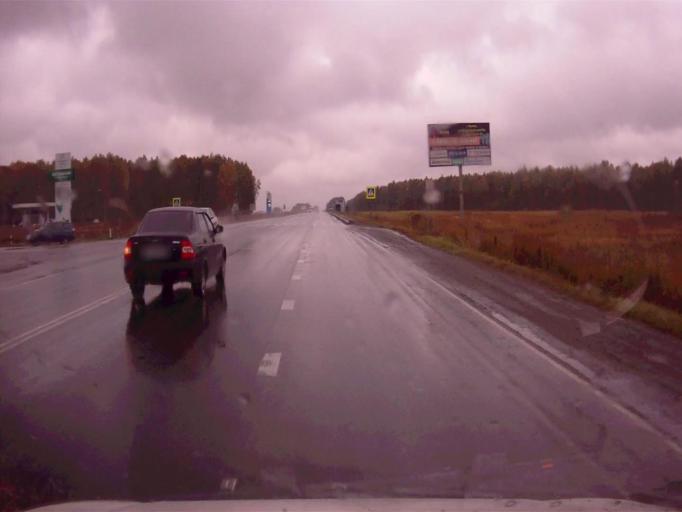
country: RU
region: Chelyabinsk
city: Argayash
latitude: 55.4173
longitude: 61.0254
